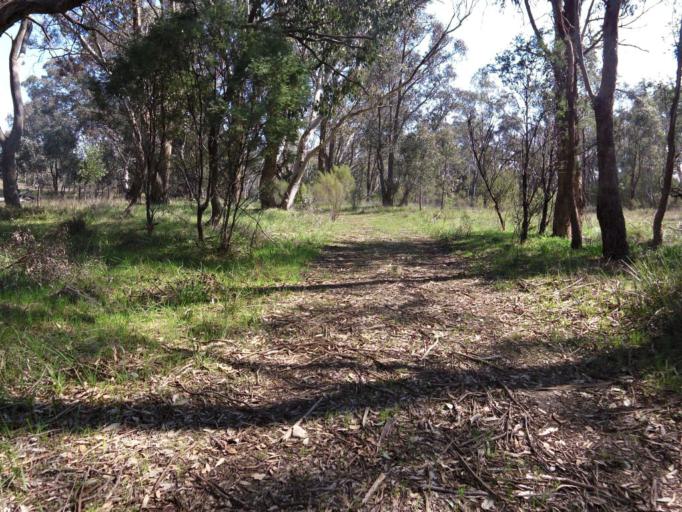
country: AU
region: Victoria
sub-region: Murrindindi
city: Alexandra
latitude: -36.9783
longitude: 145.7090
